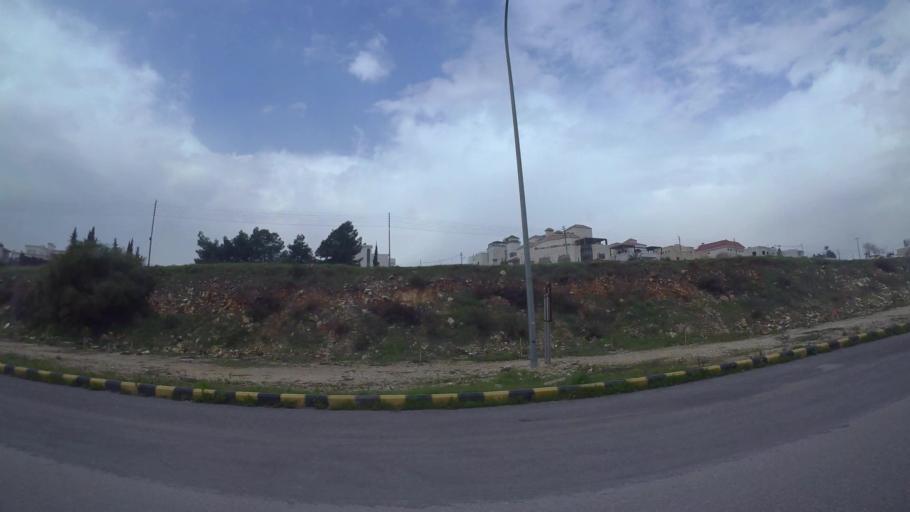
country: JO
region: Amman
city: Umm as Summaq
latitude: 31.9139
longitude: 35.8582
